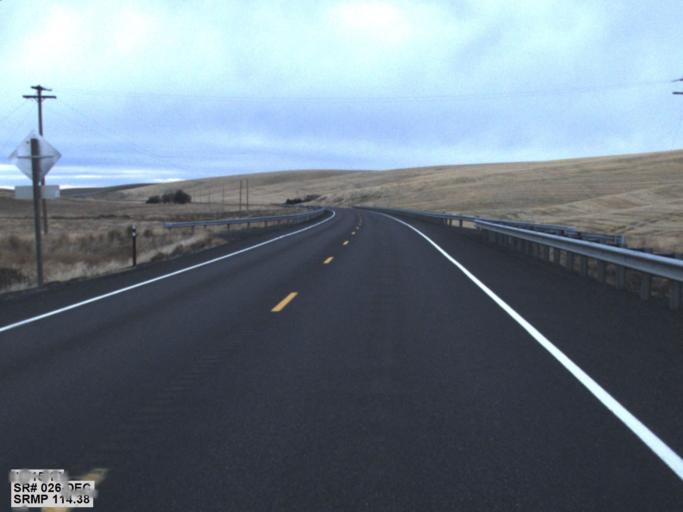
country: US
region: Washington
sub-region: Whitman County
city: Colfax
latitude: 46.8106
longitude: -117.7049
